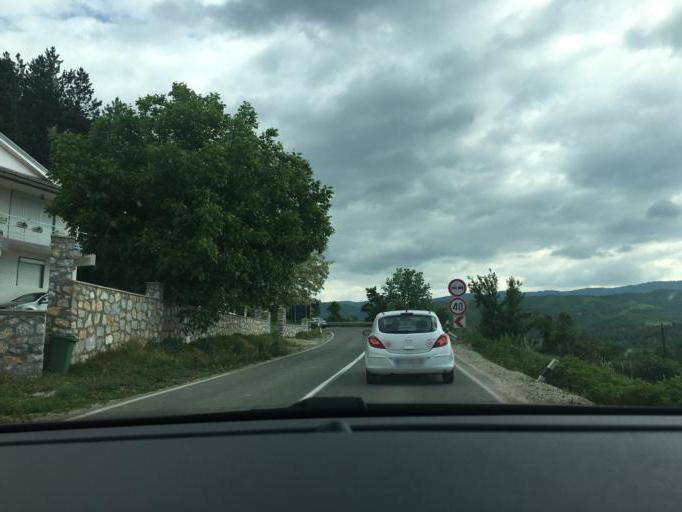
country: MK
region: Resen
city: Jankovec
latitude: 41.1126
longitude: 21.0123
